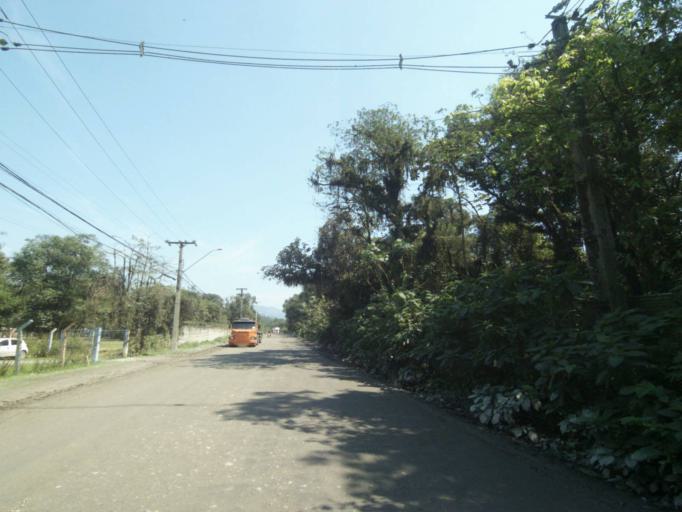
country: BR
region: Parana
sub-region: Paranagua
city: Paranagua
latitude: -25.5460
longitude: -48.5711
